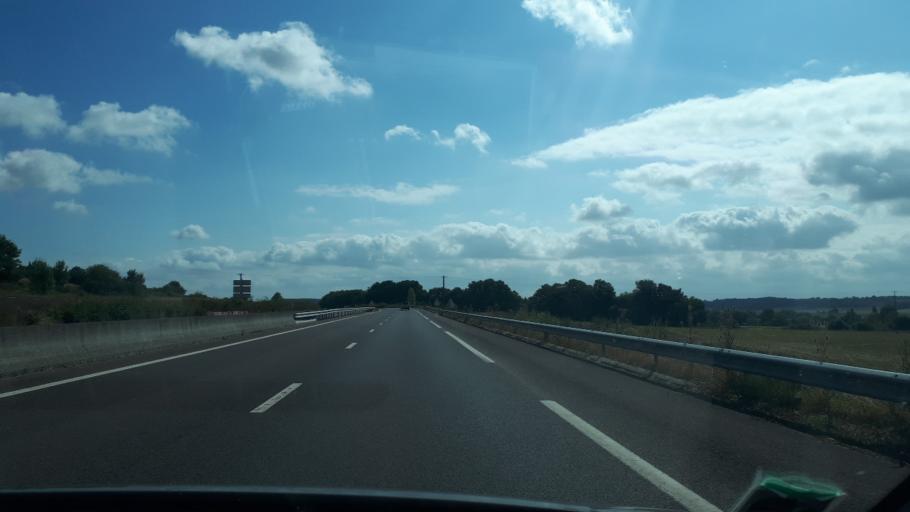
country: FR
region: Centre
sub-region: Departement du Loir-et-Cher
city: La Ville-aux-Clercs
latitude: 47.8744
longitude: 1.1485
